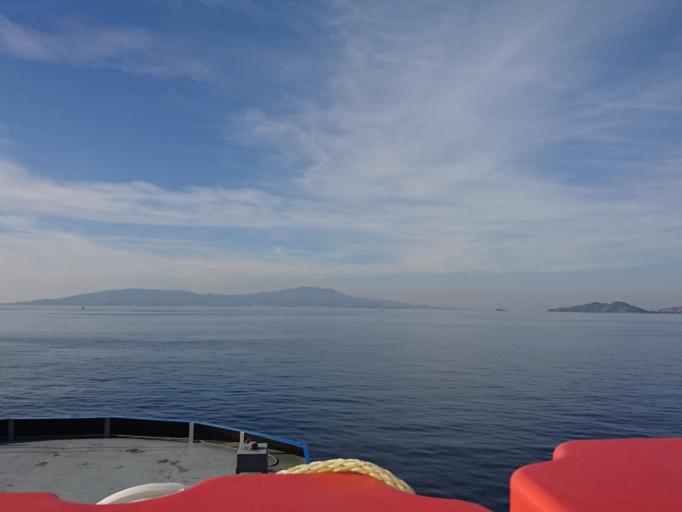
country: TR
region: Mugla
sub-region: Bodrum
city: Bodrum
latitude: 36.9921
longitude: 27.3940
